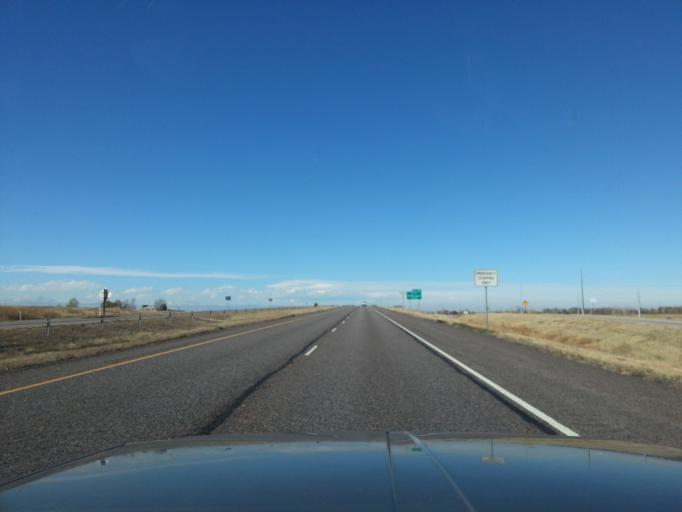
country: US
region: Colorado
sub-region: Adams County
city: Brighton
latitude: 39.9107
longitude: -104.7790
